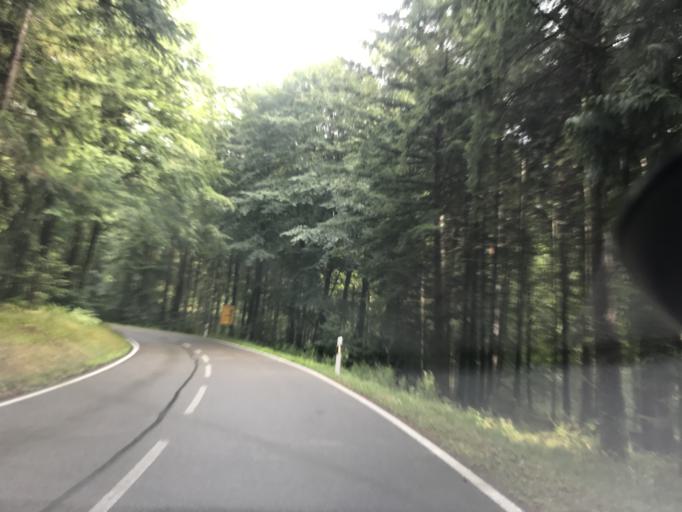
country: DE
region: Baden-Wuerttemberg
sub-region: Freiburg Region
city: Kandern
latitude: 47.7039
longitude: 7.7036
